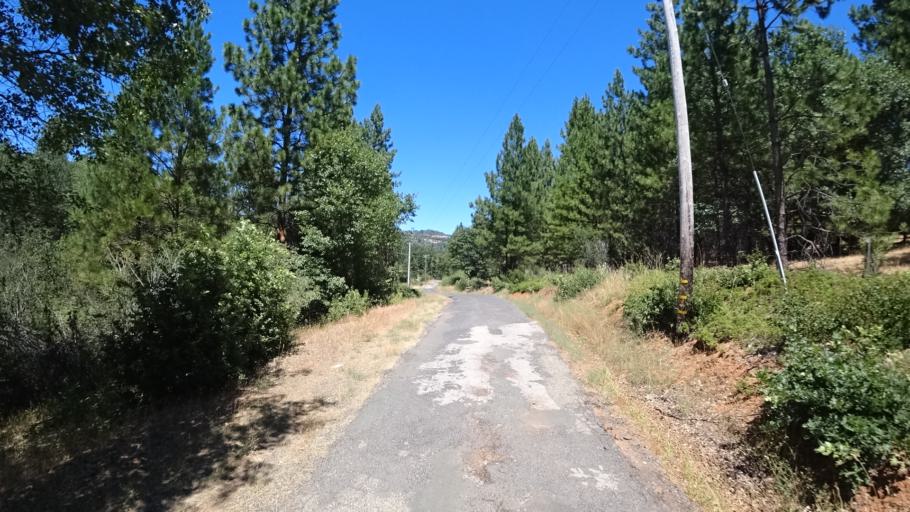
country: US
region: California
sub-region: Calaveras County
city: Mountain Ranch
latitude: 38.2712
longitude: -120.4651
